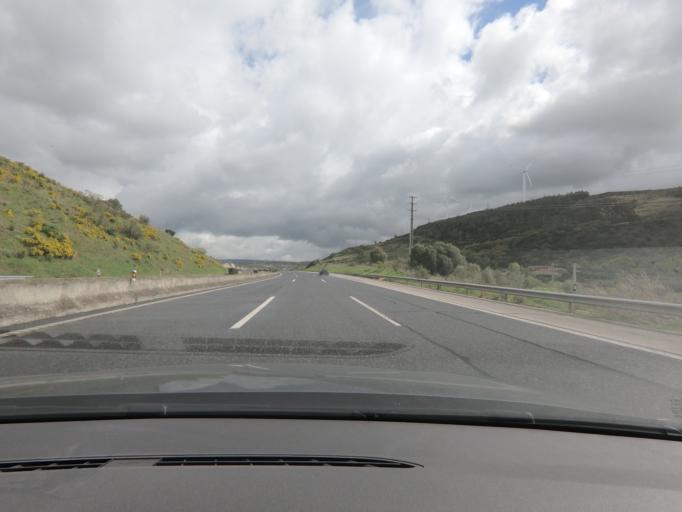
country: PT
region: Lisbon
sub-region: Loures
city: Bucelas
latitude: 38.8860
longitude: -9.1283
